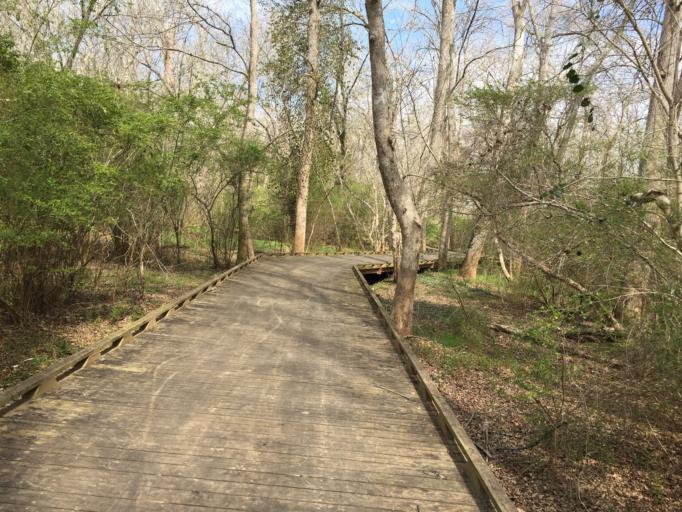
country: US
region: South Carolina
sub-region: Greenville County
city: Mauldin
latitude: 34.7909
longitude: -82.3657
